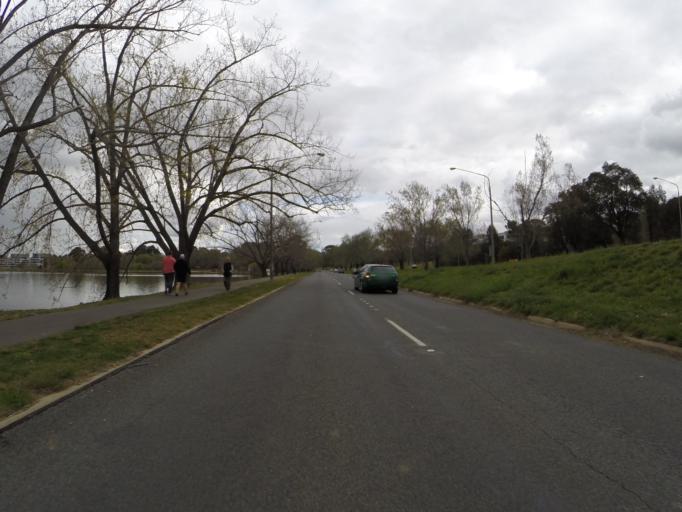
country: AU
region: Australian Capital Territory
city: Forrest
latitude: -35.3050
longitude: 149.1403
